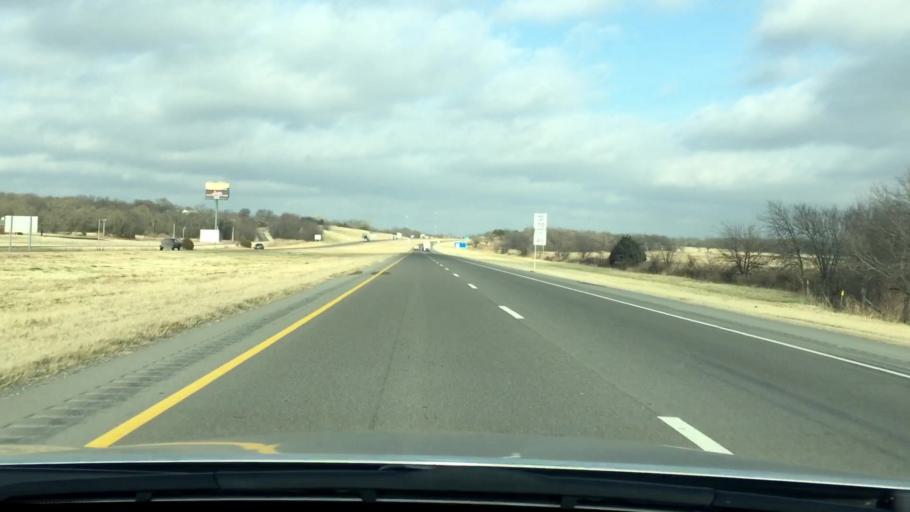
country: US
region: Oklahoma
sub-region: Garvin County
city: Pauls Valley
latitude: 34.7464
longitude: -97.2697
